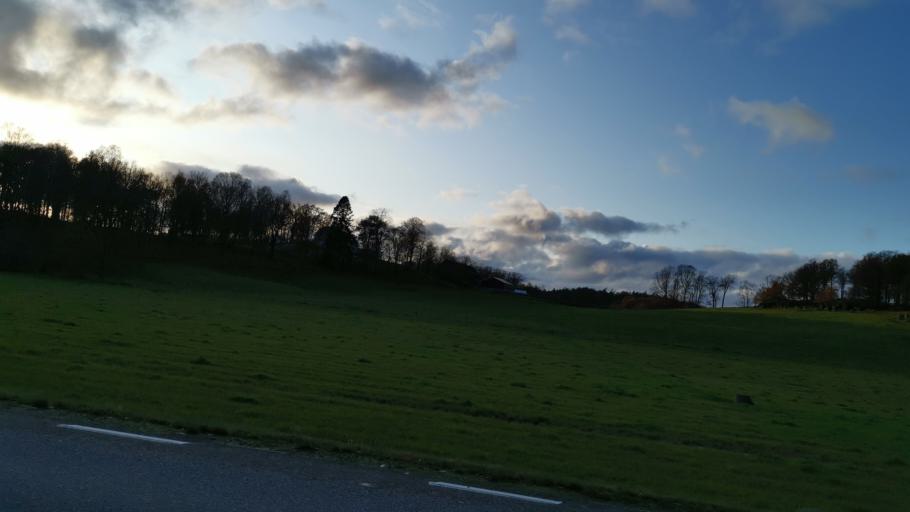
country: SE
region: Vaestra Goetaland
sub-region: Munkedals Kommun
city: Munkedal
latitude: 58.4709
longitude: 11.6602
